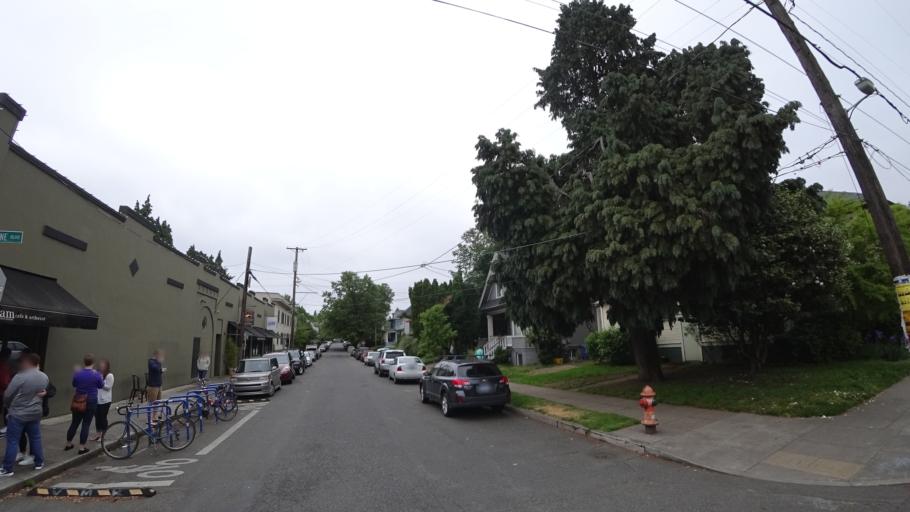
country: US
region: Oregon
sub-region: Multnomah County
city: Portland
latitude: 45.5121
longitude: -122.6426
